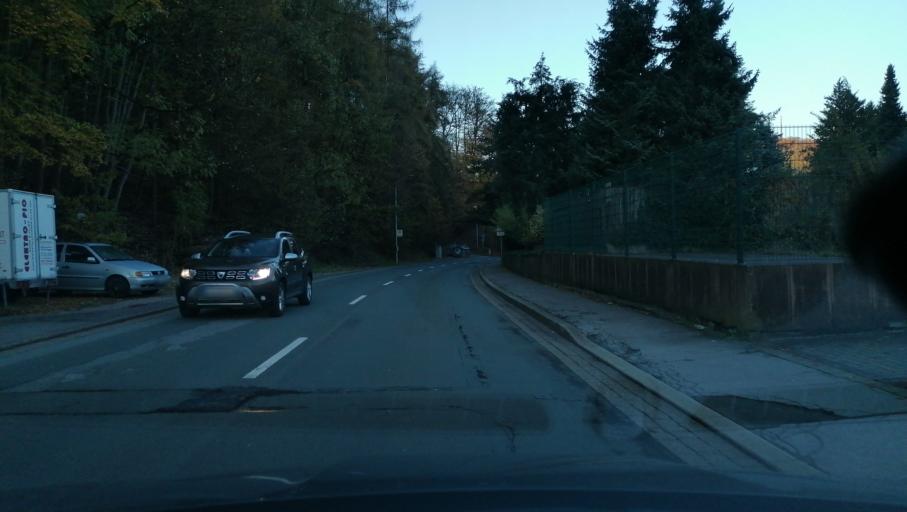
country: DE
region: North Rhine-Westphalia
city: Ennepetal
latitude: 51.2886
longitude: 7.3392
